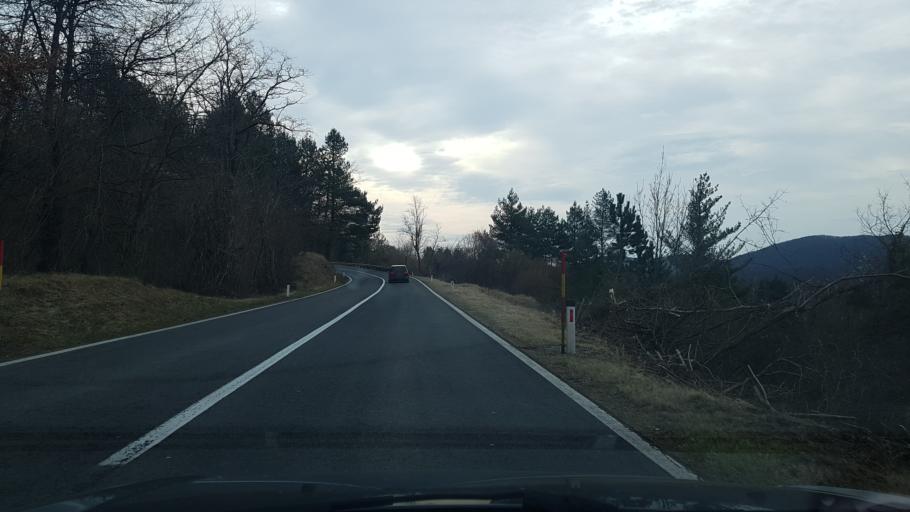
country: SI
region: Ilirska Bistrica
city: Ilirska Bistrica
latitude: 45.5019
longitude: 14.1790
